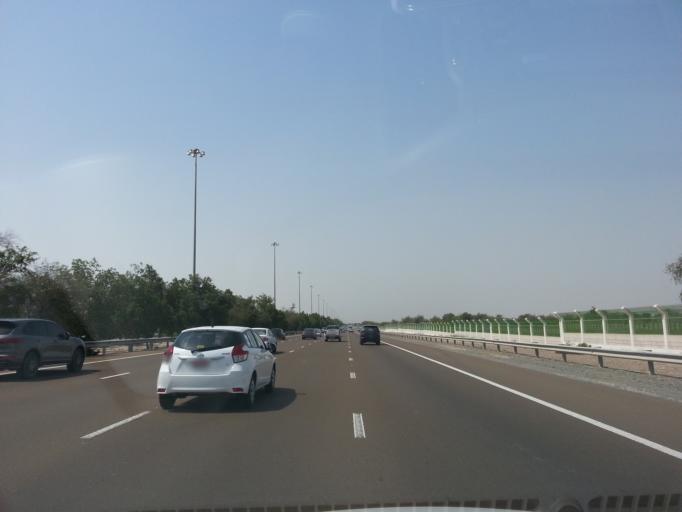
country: AE
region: Dubai
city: Dubai
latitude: 24.7535
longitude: 54.8368
